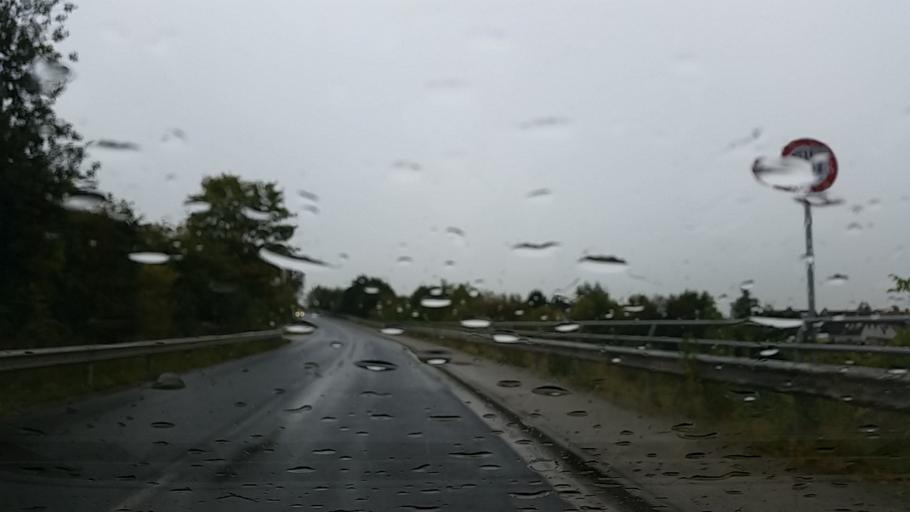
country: DE
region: Lower Saxony
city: Leiferde
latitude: 52.2081
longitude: 10.4992
